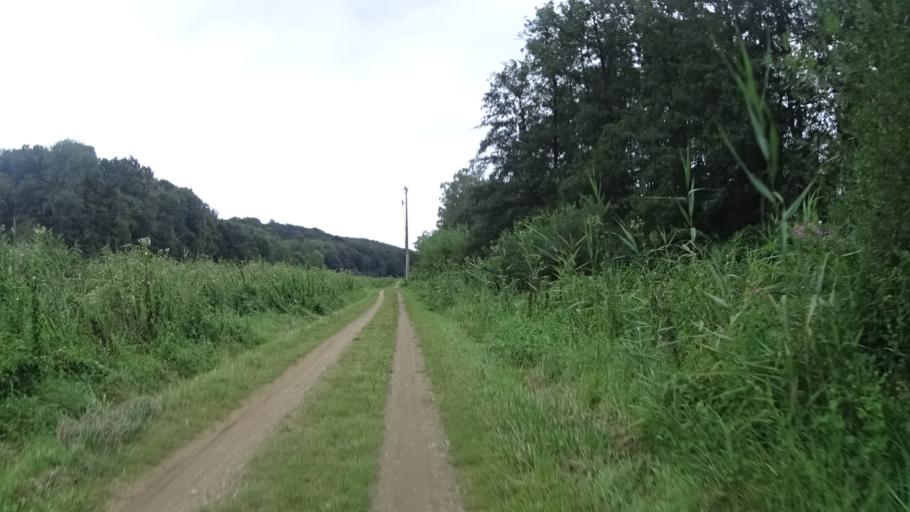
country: DE
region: Schleswig-Holstein
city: Alt Molln
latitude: 53.6391
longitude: 10.6598
